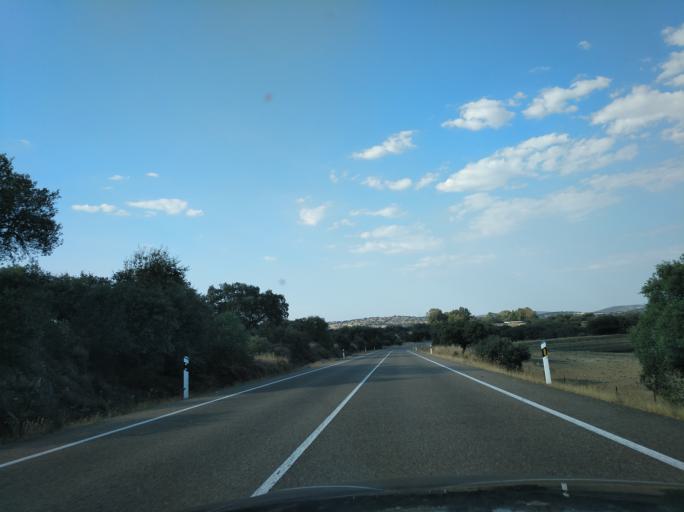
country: ES
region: Extremadura
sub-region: Provincia de Badajoz
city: Alconchel
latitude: 38.4532
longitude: -7.0831
